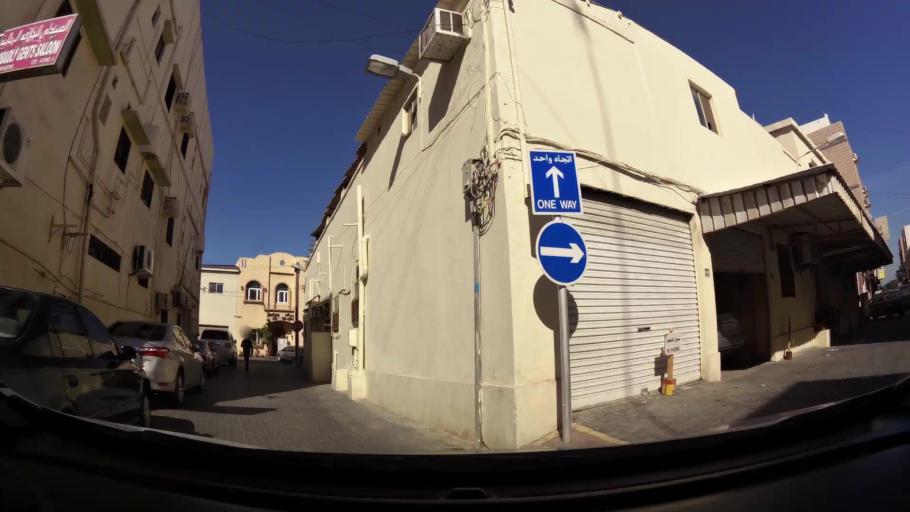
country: BH
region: Muharraq
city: Al Muharraq
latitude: 26.2602
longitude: 50.6122
